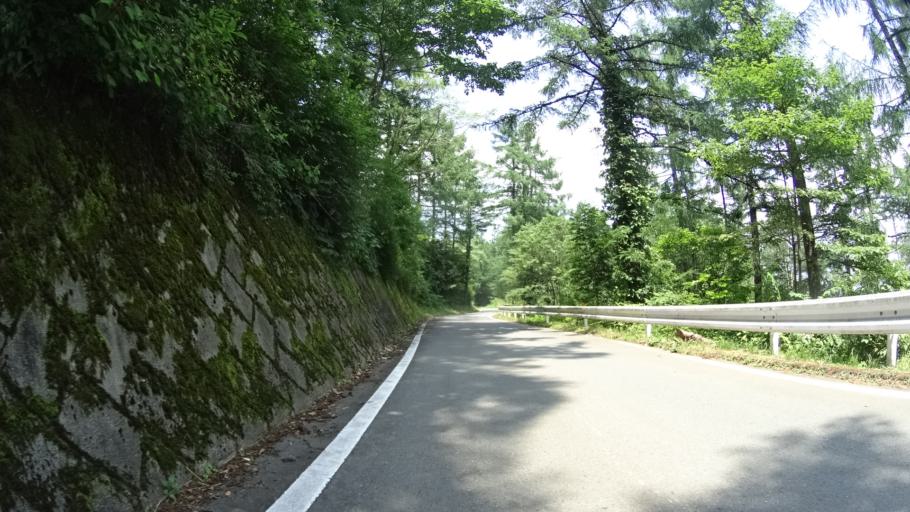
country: JP
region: Nagano
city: Saku
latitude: 36.0989
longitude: 138.6560
